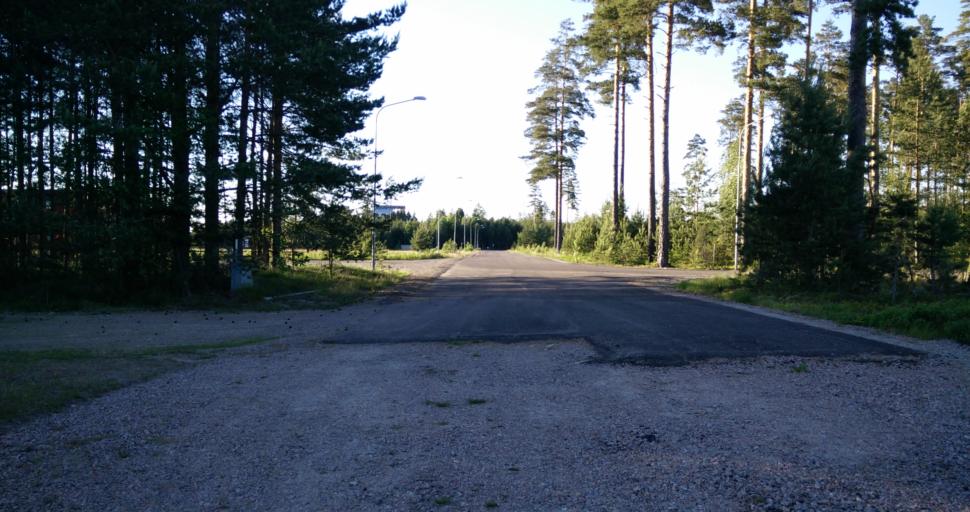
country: SE
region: Vaermland
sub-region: Hagfors Kommun
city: Hagfors
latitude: 60.0240
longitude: 13.5843
